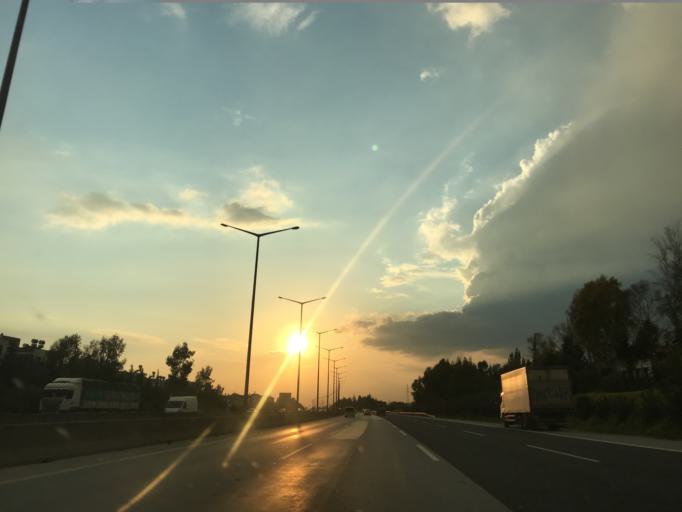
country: TR
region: Adana
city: Seyhan
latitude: 37.0325
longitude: 35.2425
